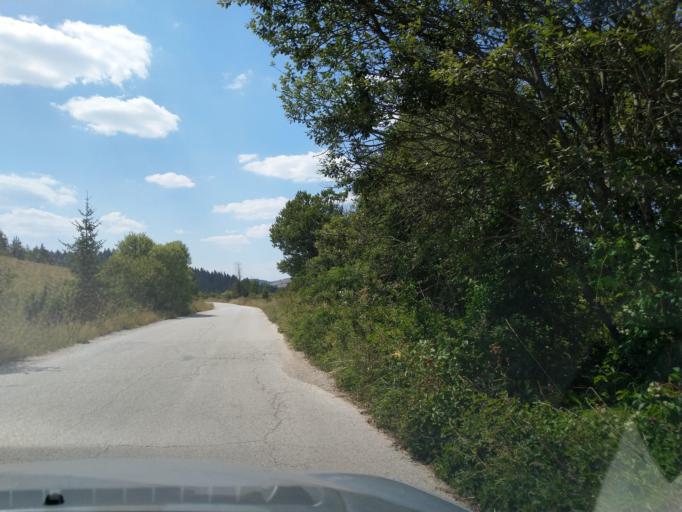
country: RS
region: Central Serbia
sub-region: Zlatiborski Okrug
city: Nova Varos
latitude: 43.4468
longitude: 19.9615
